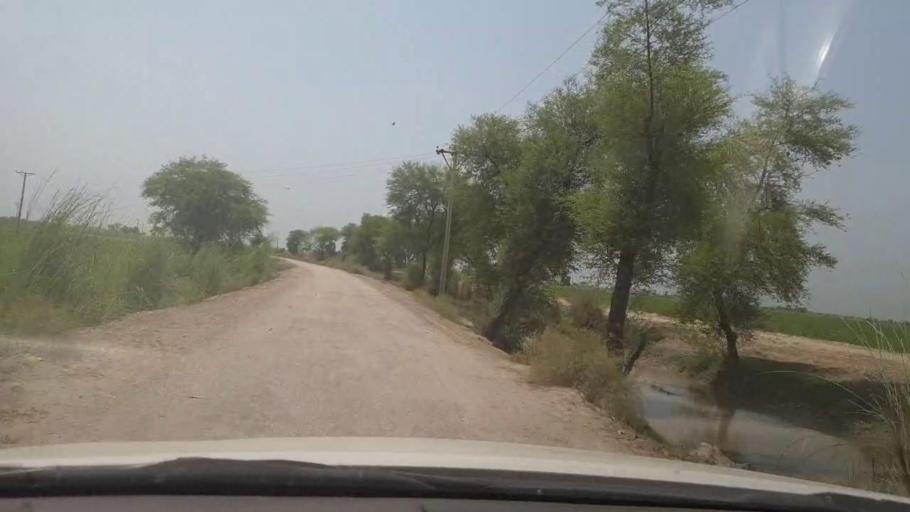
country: PK
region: Sindh
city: Shikarpur
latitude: 28.0514
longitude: 68.5885
